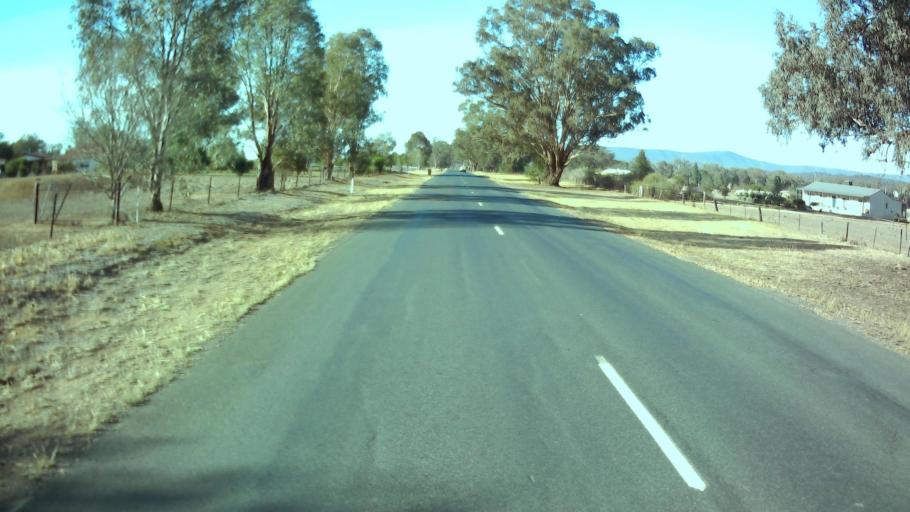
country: AU
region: New South Wales
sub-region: Weddin
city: Grenfell
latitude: -33.9094
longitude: 148.1454
